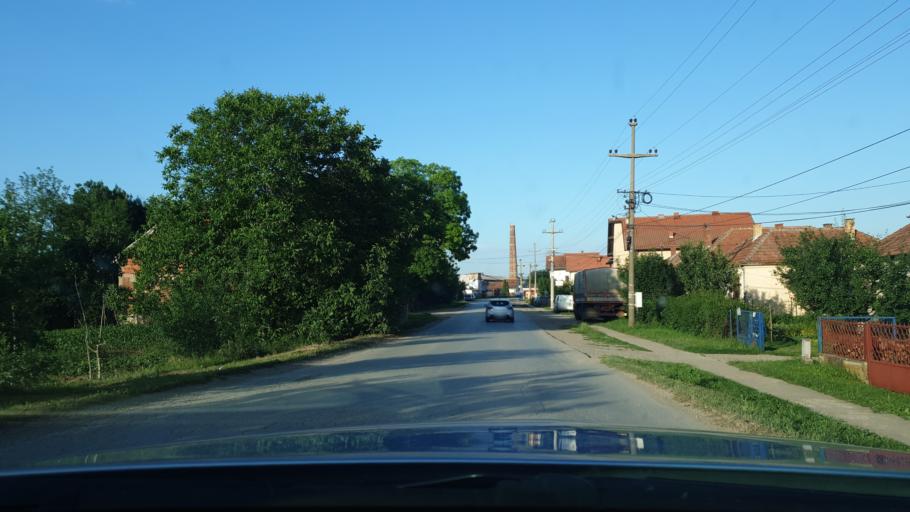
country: RS
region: Central Serbia
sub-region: Podunavski Okrug
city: Velika Plana
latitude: 44.3415
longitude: 21.0972
